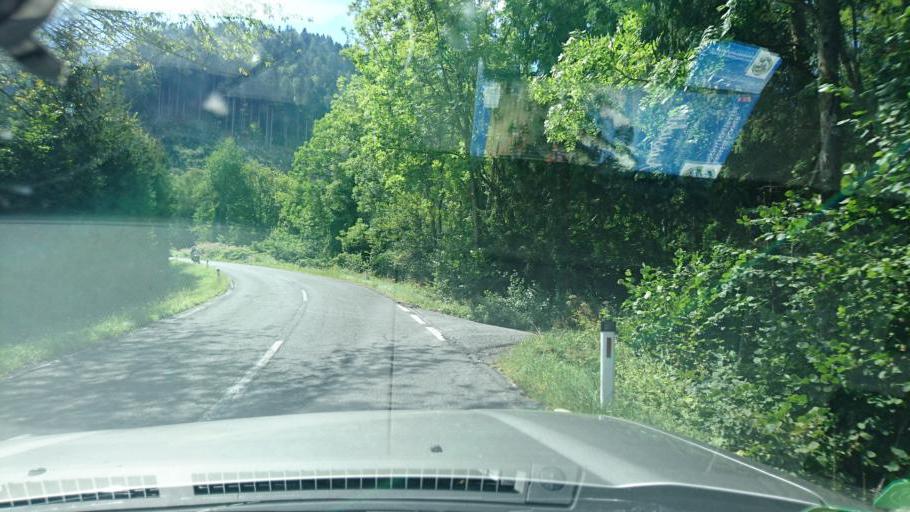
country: AT
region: Carinthia
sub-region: Politischer Bezirk Villach Land
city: Arnoldstein
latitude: 46.5407
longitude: 13.7724
